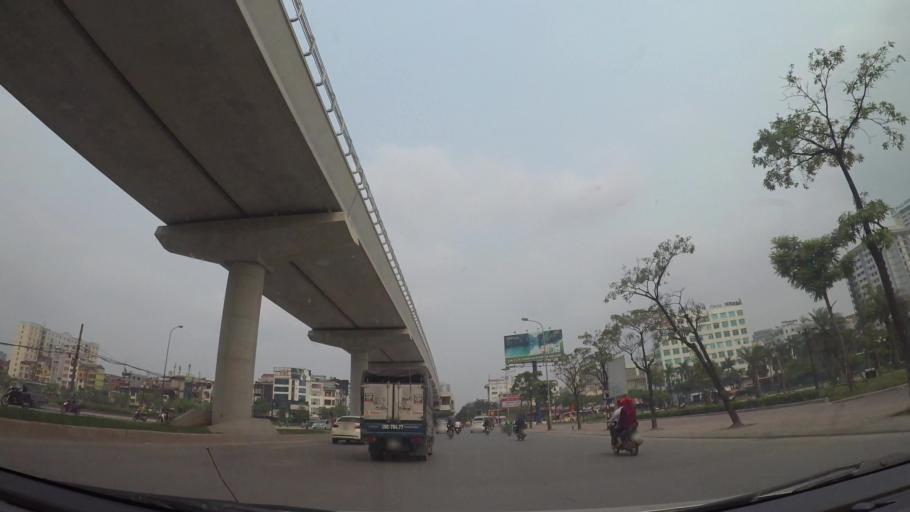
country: VN
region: Ha Noi
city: Cau Dien
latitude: 21.0385
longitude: 105.7708
